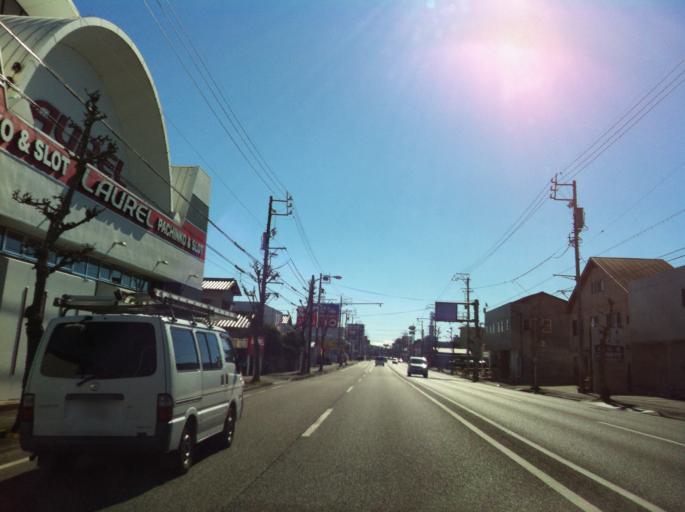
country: JP
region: Shizuoka
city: Shizuoka-shi
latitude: 35.0057
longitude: 138.4041
